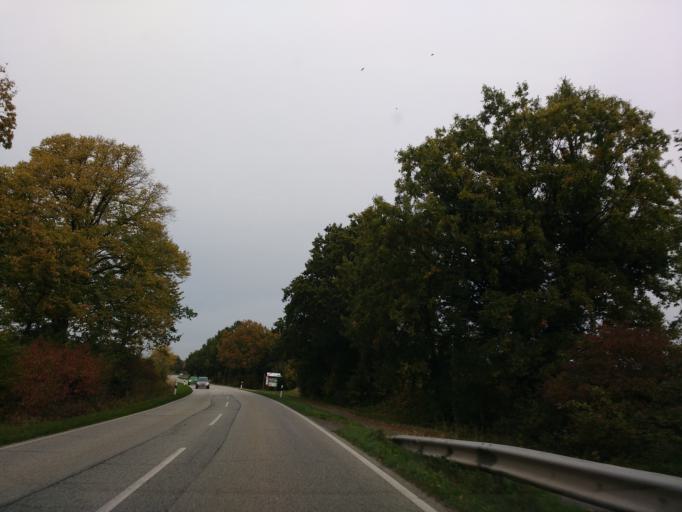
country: DE
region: Schleswig-Holstein
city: Gromitz
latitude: 54.1596
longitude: 10.9640
